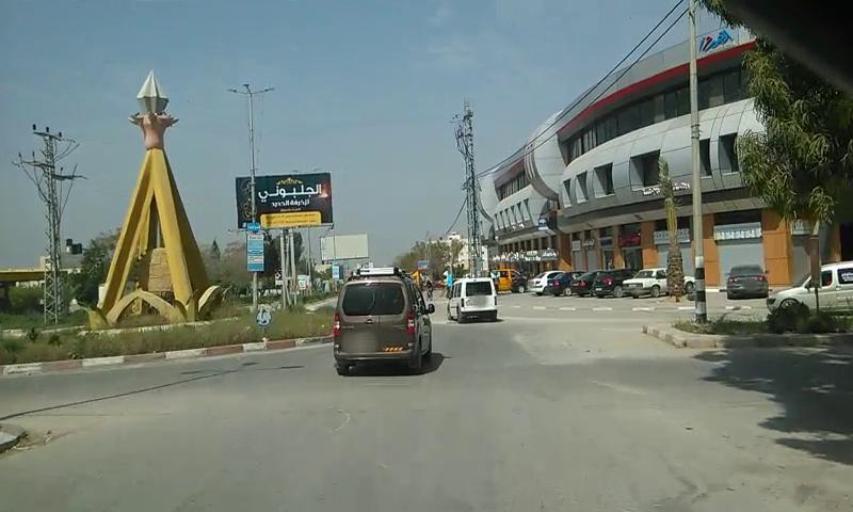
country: PS
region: West Bank
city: Janin
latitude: 32.4703
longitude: 35.3037
